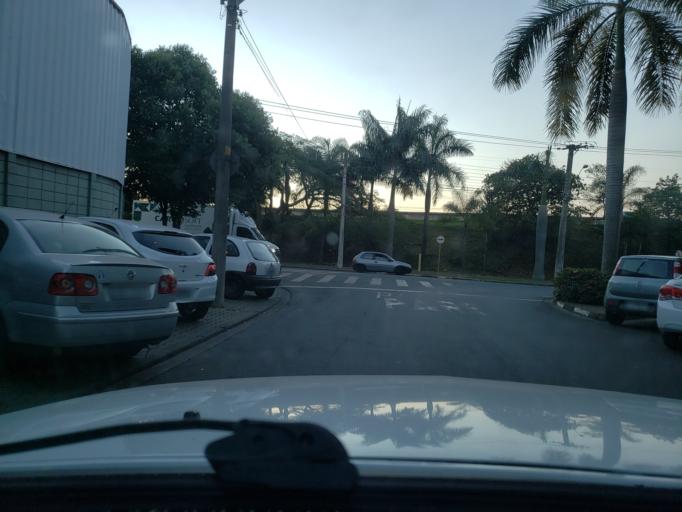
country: BR
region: Sao Paulo
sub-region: Moji-Guacu
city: Mogi-Gaucu
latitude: -22.3454
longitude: -46.9490
